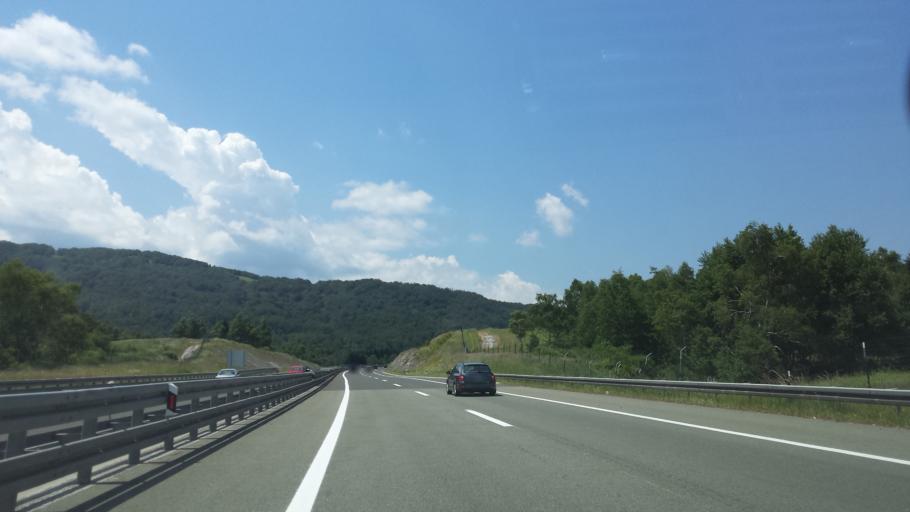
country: HR
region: Primorsko-Goranska
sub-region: Grad Delnice
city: Delnice
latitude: 45.3847
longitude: 14.8867
